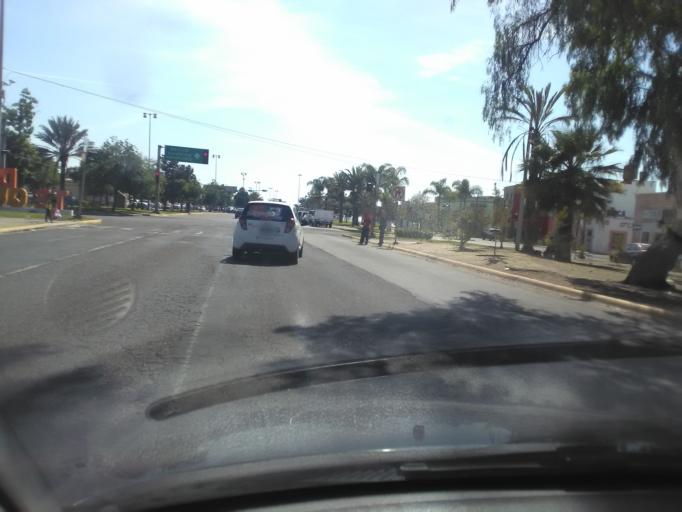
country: MX
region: Durango
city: Victoria de Durango
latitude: 24.0199
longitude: -104.6683
